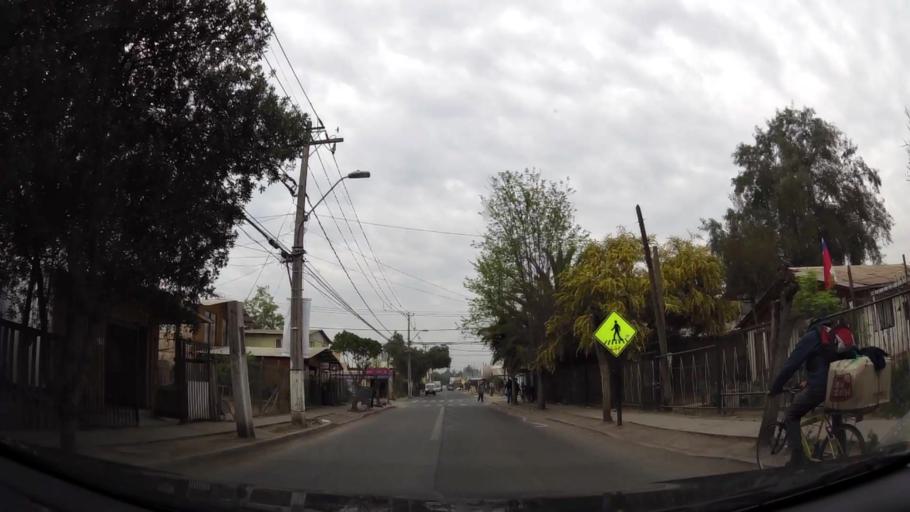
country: CL
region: Santiago Metropolitan
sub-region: Provincia de Chacabuco
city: Lampa
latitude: -33.2329
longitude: -70.8073
